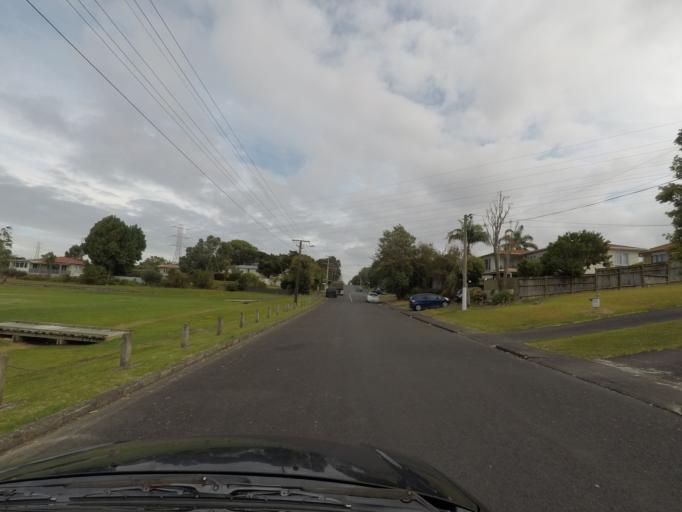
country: NZ
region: Auckland
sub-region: Auckland
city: Rosebank
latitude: -36.8948
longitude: 174.6694
